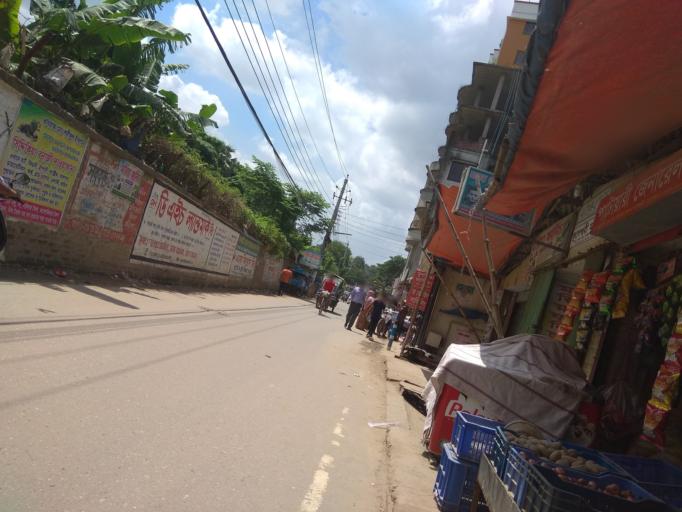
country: BD
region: Dhaka
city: Tungi
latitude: 23.8311
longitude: 90.3899
